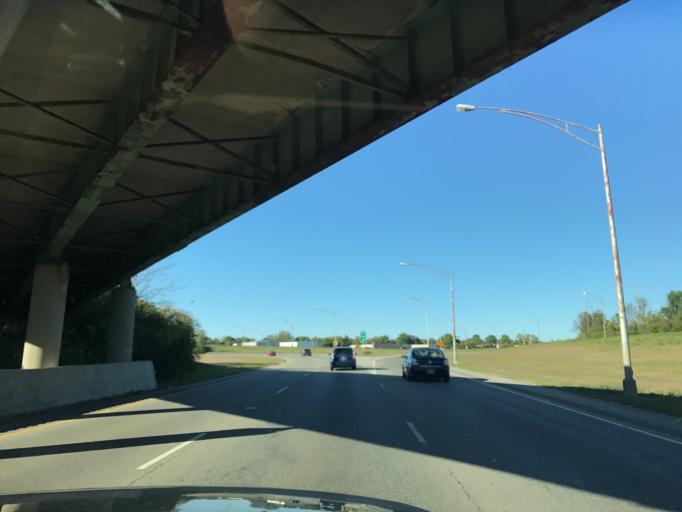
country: US
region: Ohio
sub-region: Franklin County
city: Bexley
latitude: 39.9211
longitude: -82.9200
